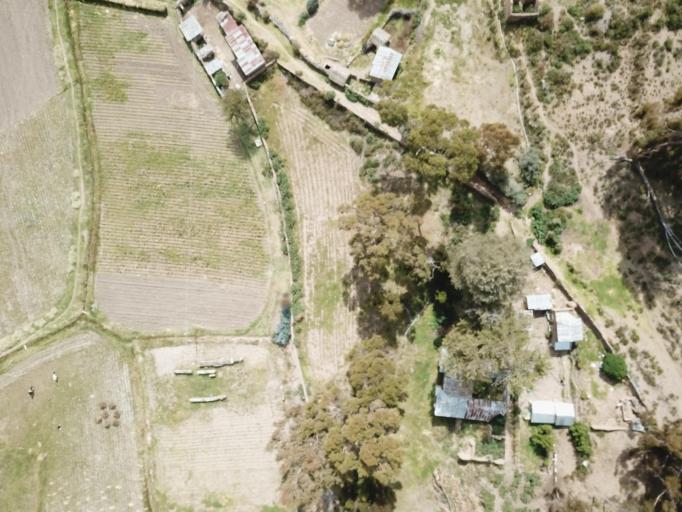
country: BO
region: La Paz
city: Achacachi
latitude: -16.0575
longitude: -68.8098
